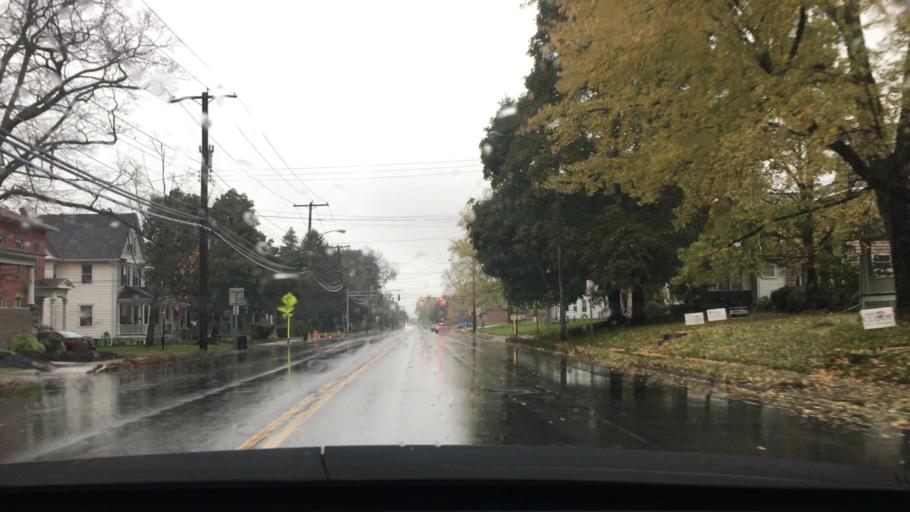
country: US
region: New York
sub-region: Cayuga County
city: Auburn
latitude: 42.9393
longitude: -76.5667
